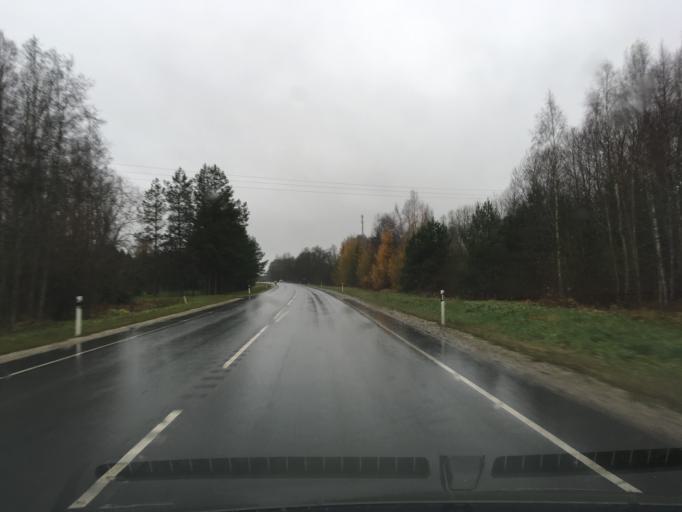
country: EE
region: Harju
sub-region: Nissi vald
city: Turba
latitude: 58.8899
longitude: 24.0938
